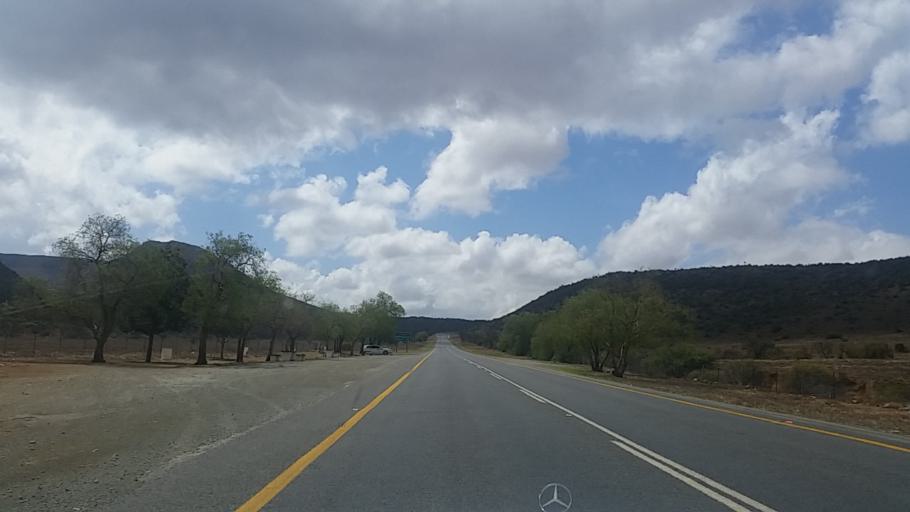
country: ZA
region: Eastern Cape
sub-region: Cacadu District Municipality
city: Graaff-Reinet
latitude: -32.0700
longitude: 24.6055
